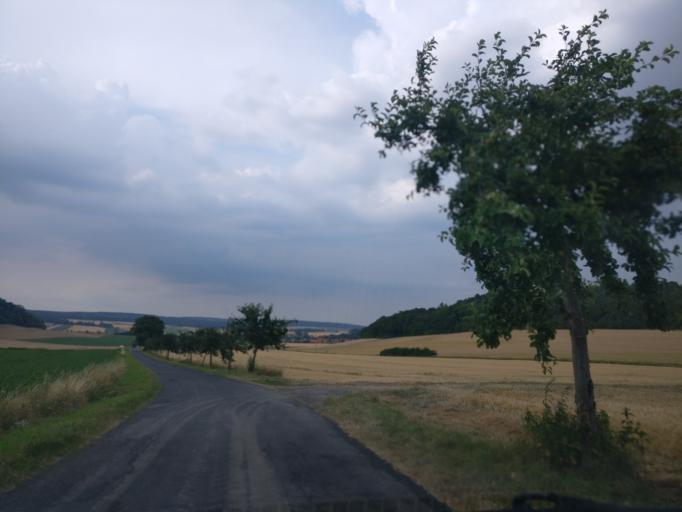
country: DE
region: Lower Saxony
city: Adelebsen
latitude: 51.5812
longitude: 9.7808
